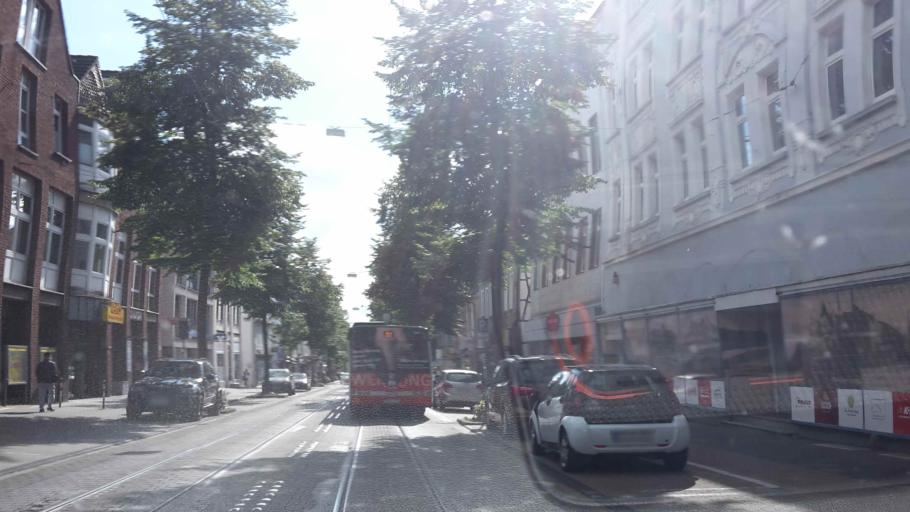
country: DE
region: North Rhine-Westphalia
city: Hattingen
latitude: 51.4290
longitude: 7.1661
